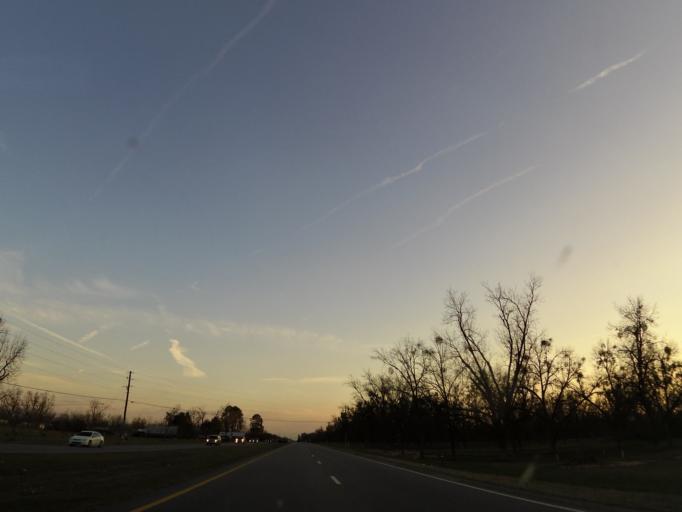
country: US
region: Georgia
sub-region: Lee County
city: Leesburg
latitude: 31.6893
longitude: -84.1730
